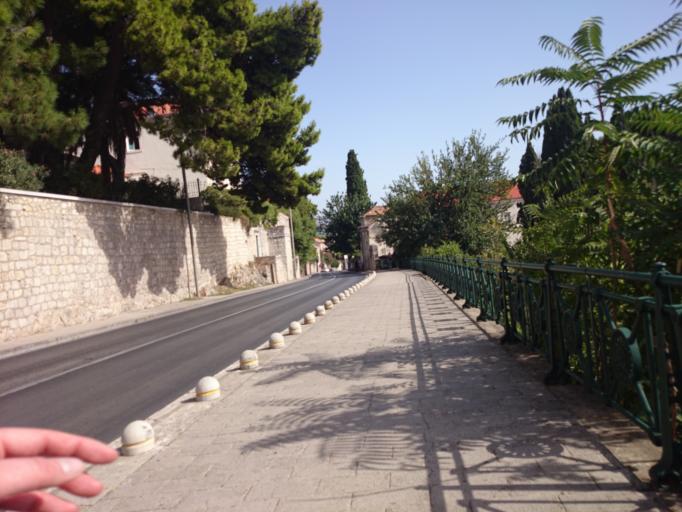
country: HR
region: Dubrovacko-Neretvanska
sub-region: Grad Dubrovnik
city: Dubrovnik
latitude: 42.6448
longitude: 18.0990
